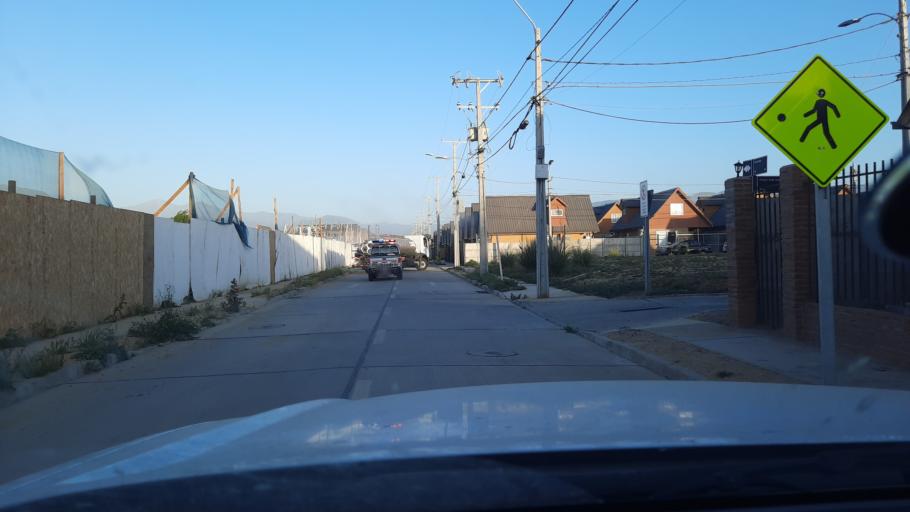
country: CL
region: Valparaiso
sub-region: Provincia de Marga Marga
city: Limache
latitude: -32.9951
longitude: -71.2792
